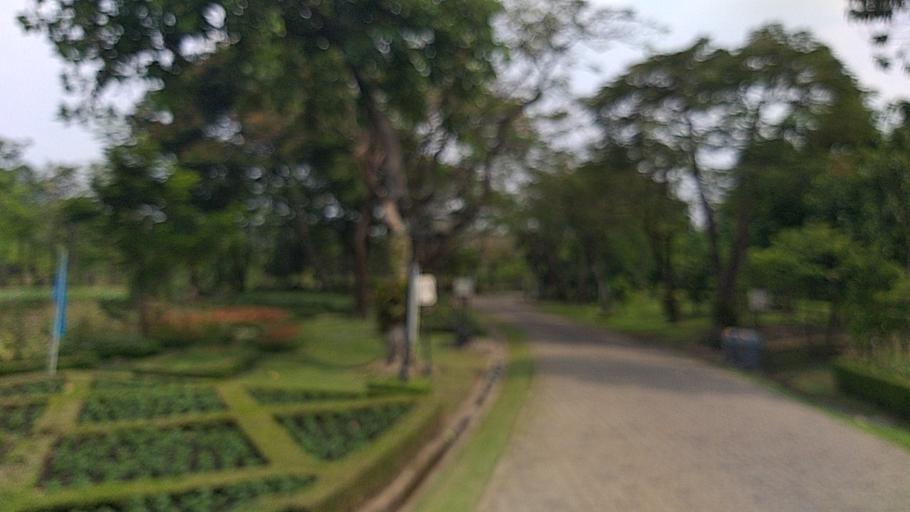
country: TH
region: Bangkok
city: Bang Sue
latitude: 13.8061
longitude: 100.5489
